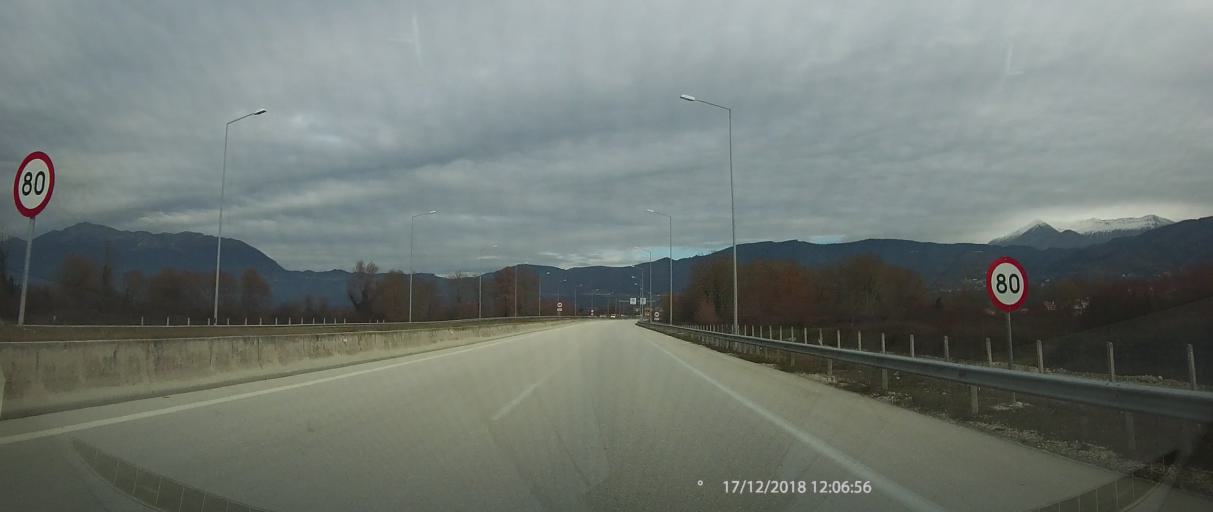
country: GR
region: Epirus
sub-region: Nomos Ioanninon
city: Koutselio
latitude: 39.6140
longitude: 20.9432
